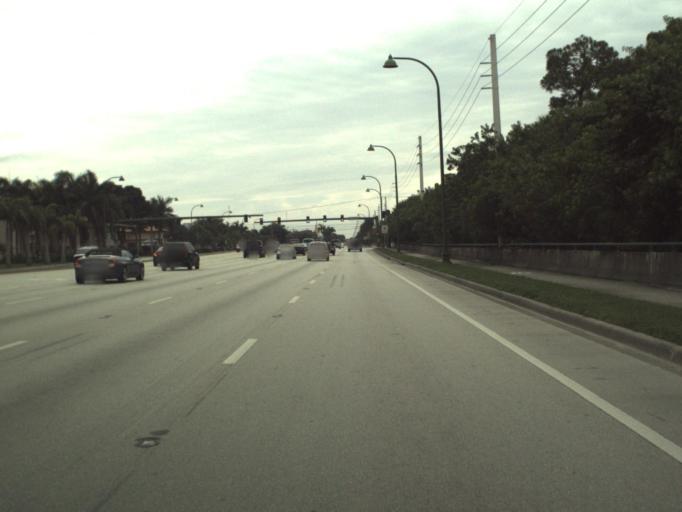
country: US
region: Florida
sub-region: Palm Beach County
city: Wellington
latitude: 26.6811
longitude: -80.2320
